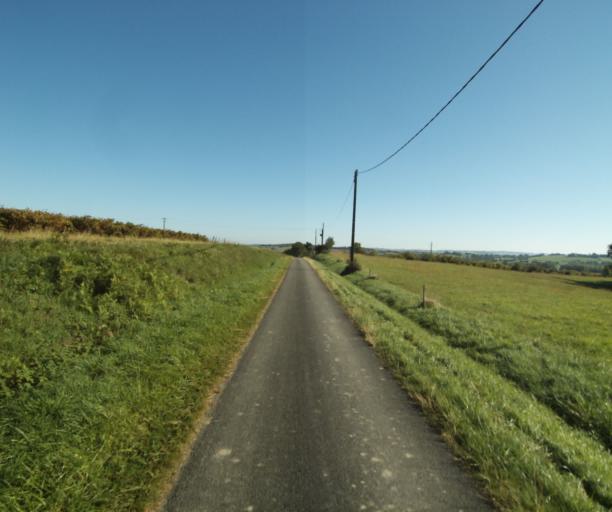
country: FR
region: Midi-Pyrenees
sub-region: Departement du Gers
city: Gondrin
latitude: 43.8200
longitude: 0.2351
